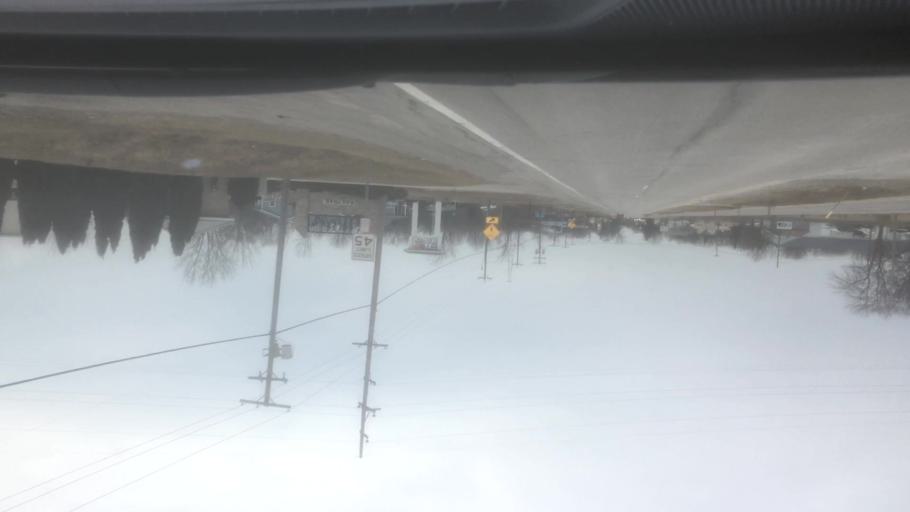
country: US
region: Michigan
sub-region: Bay County
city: Bay City
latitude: 43.5767
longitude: -83.8537
